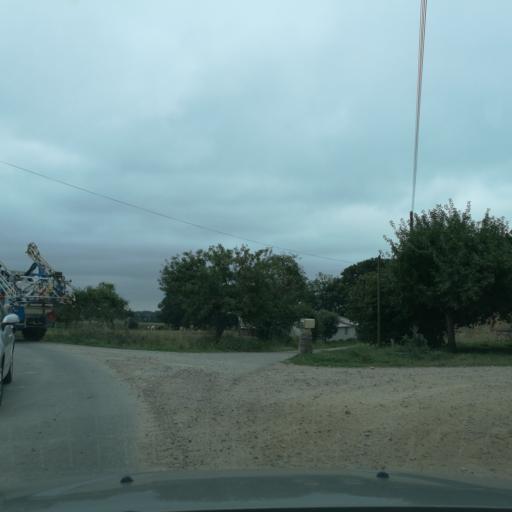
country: FR
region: Brittany
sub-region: Departement d'Ille-et-Vilaine
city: Montauban-de-Bretagne
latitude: 48.1824
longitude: -2.0029
